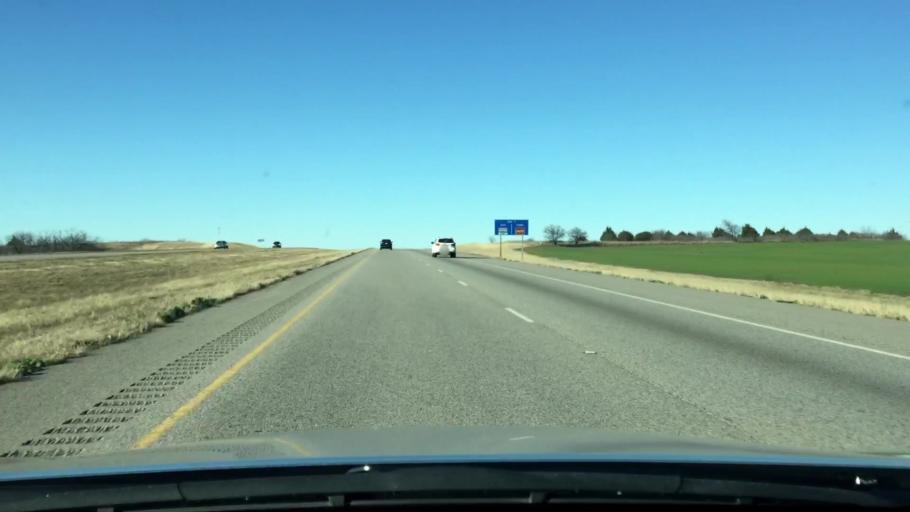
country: US
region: Texas
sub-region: Hill County
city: Itasca
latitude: 32.1391
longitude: -97.1218
